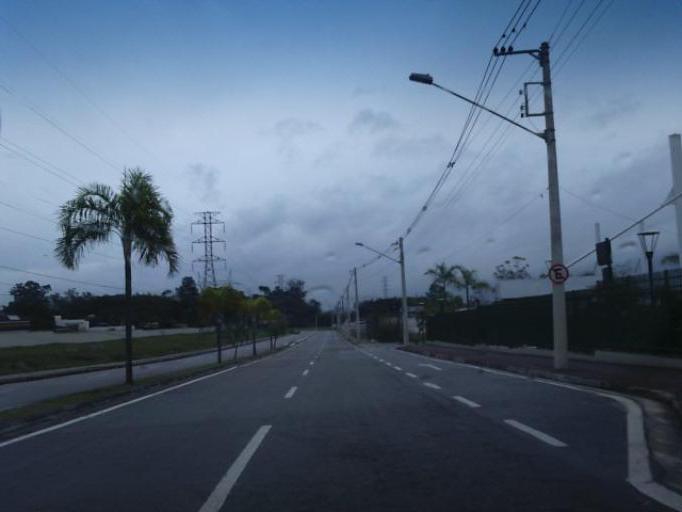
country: BR
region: Sao Paulo
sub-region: Sao Jose Dos Campos
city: Sao Jose dos Campos
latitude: -23.2030
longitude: -45.9108
